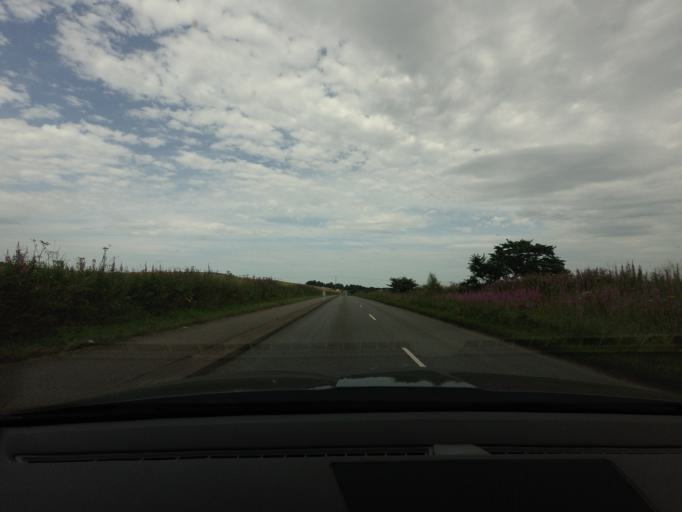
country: GB
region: Scotland
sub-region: Highland
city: Alness
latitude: 57.6847
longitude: -4.2888
